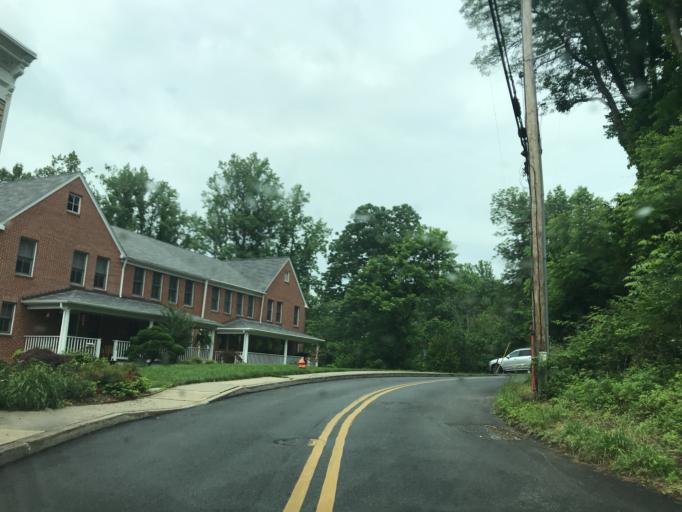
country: US
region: Maryland
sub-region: Howard County
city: Ellicott City
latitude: 39.2763
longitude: -76.7870
